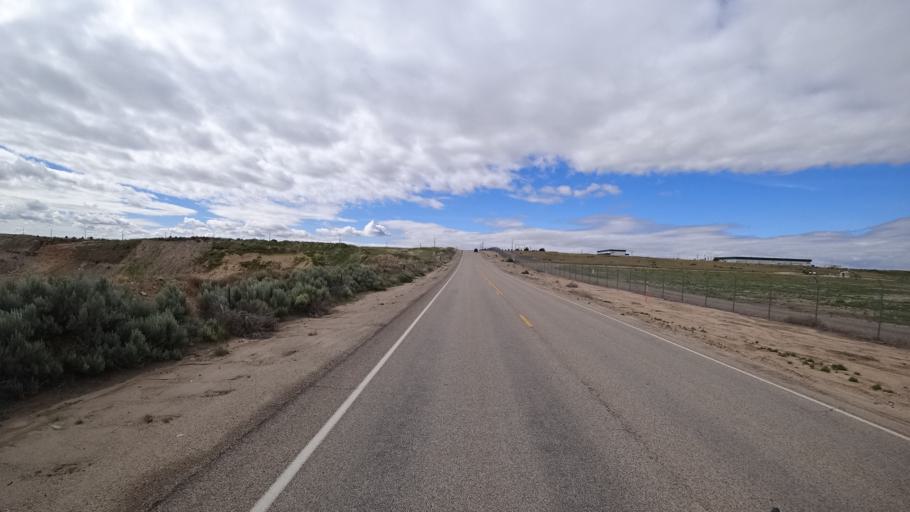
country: US
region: Idaho
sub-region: Ada County
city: Boise
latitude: 43.5506
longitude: -116.1876
